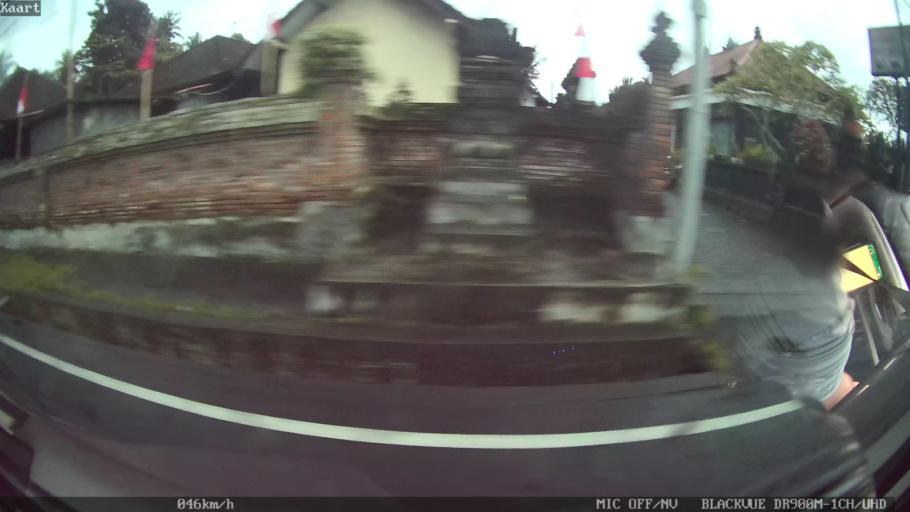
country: ID
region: Bali
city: Banjar Sayanbaleran
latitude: -8.5061
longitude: 115.1875
